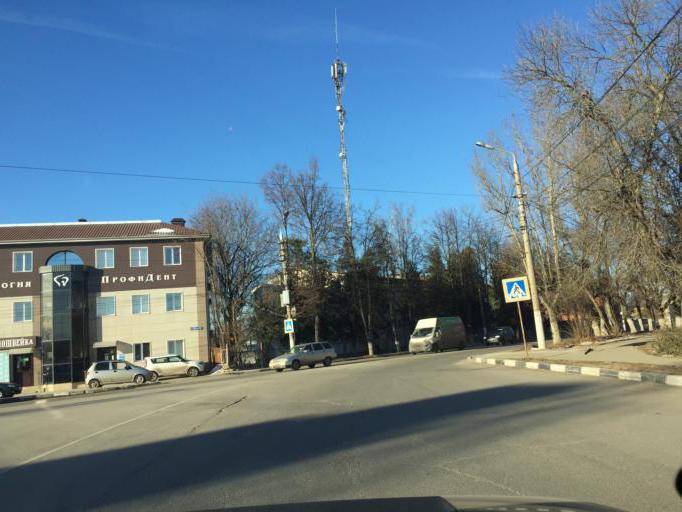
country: RU
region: Tula
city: Tula
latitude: 54.1860
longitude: 37.5724
